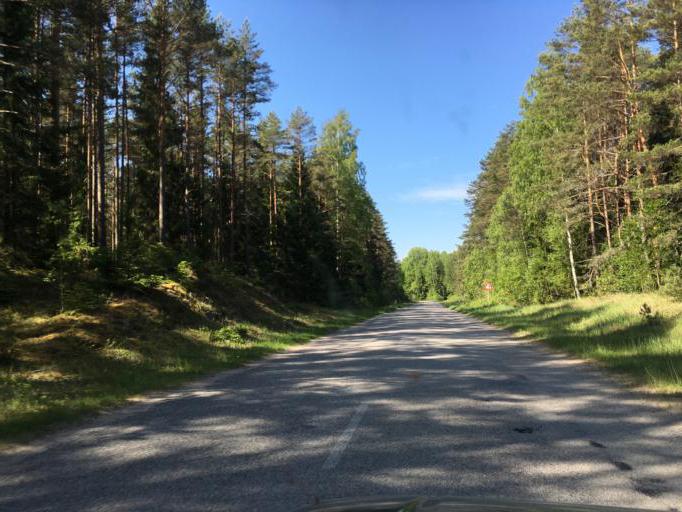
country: LV
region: Ventspils
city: Ventspils
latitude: 57.5092
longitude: 21.8537
